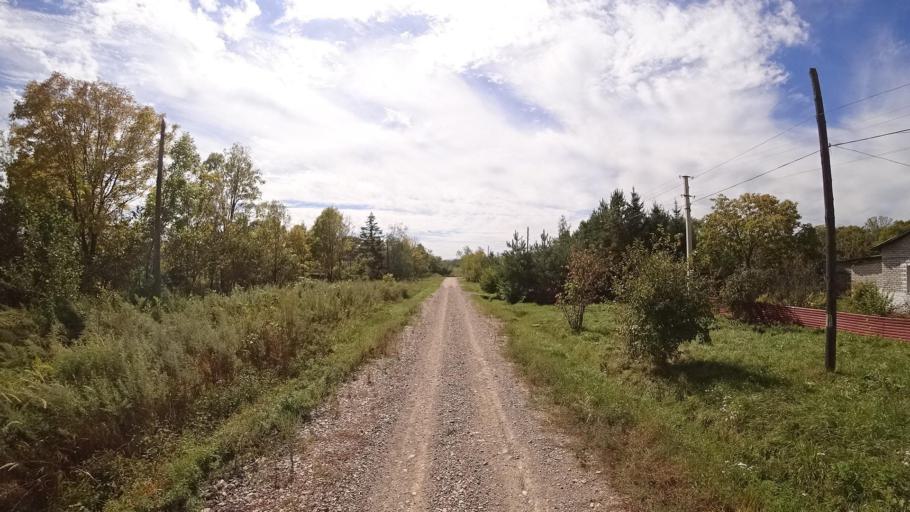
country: RU
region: Primorskiy
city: Yakovlevka
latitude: 44.6389
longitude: 133.5976
